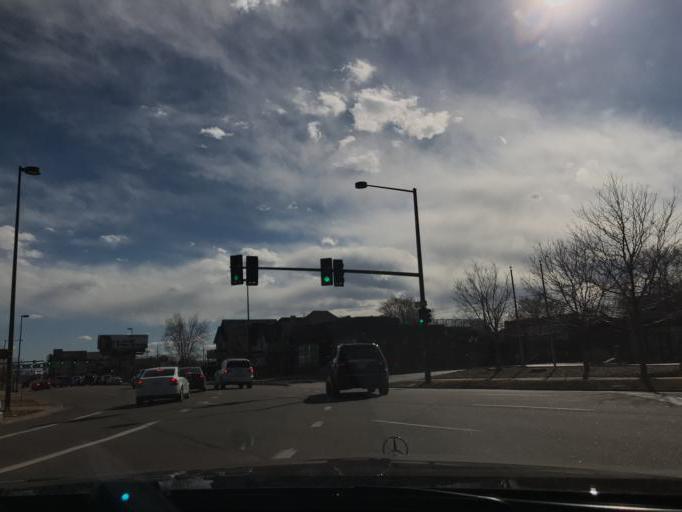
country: US
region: Colorado
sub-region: Denver County
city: Denver
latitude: 39.7288
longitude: -105.0001
